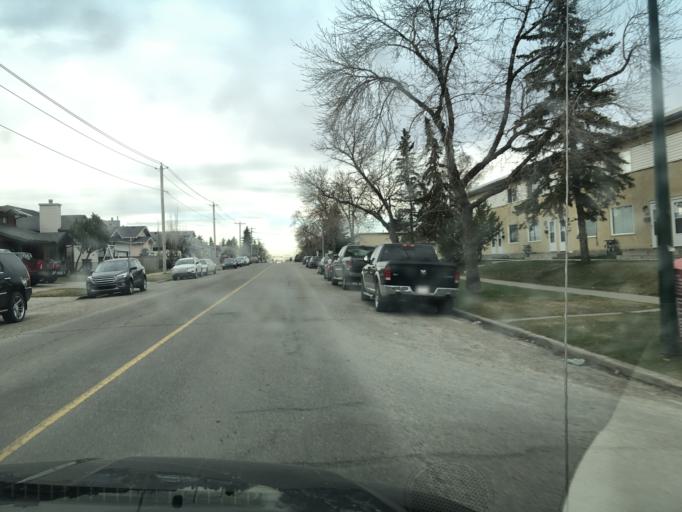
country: CA
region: Alberta
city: Calgary
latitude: 51.0729
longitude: -114.0134
